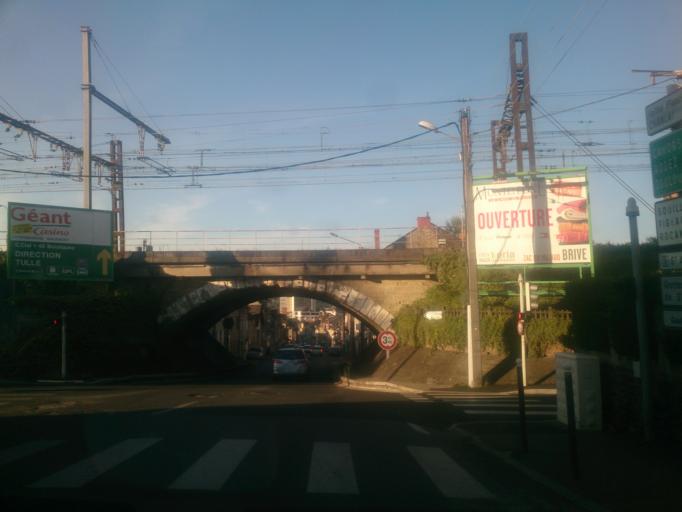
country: FR
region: Limousin
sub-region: Departement de la Correze
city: Brive-la-Gaillarde
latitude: 45.1505
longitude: 1.5318
